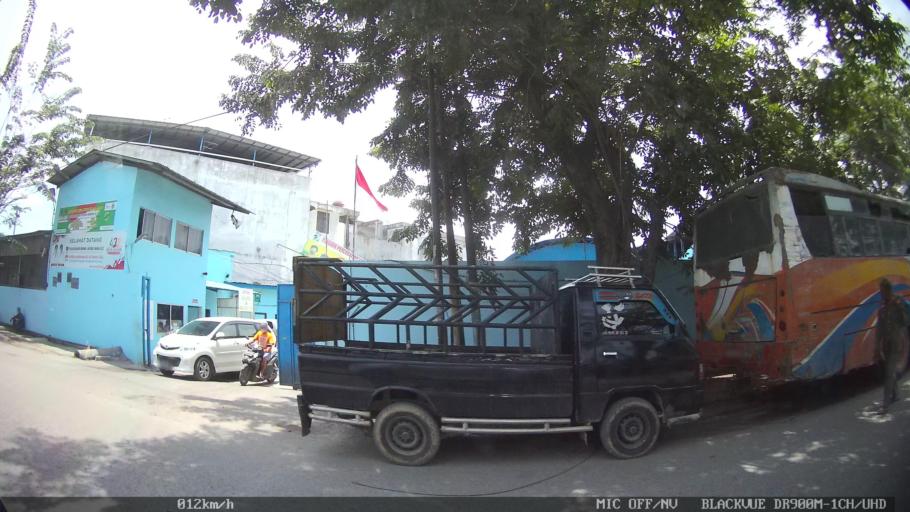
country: ID
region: North Sumatra
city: Labuhan Deli
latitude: 3.7196
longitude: 98.6693
